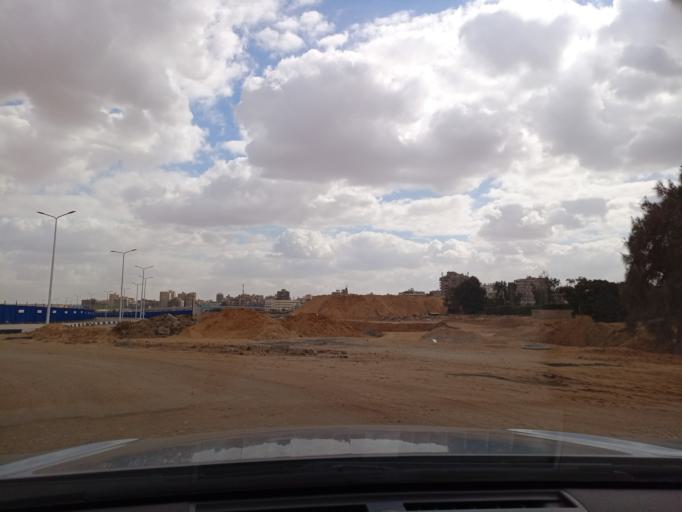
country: EG
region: Muhafazat al Qalyubiyah
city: Al Khankah
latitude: 30.1240
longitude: 31.3513
